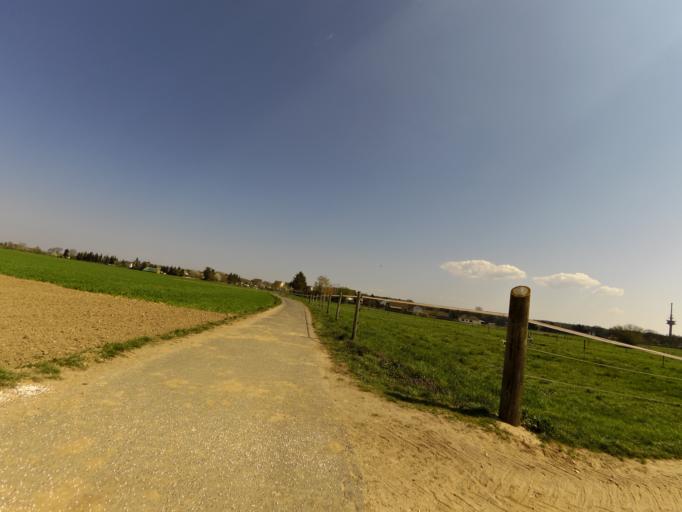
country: DE
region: North Rhine-Westphalia
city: Meckenheim
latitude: 50.6746
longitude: 7.0119
